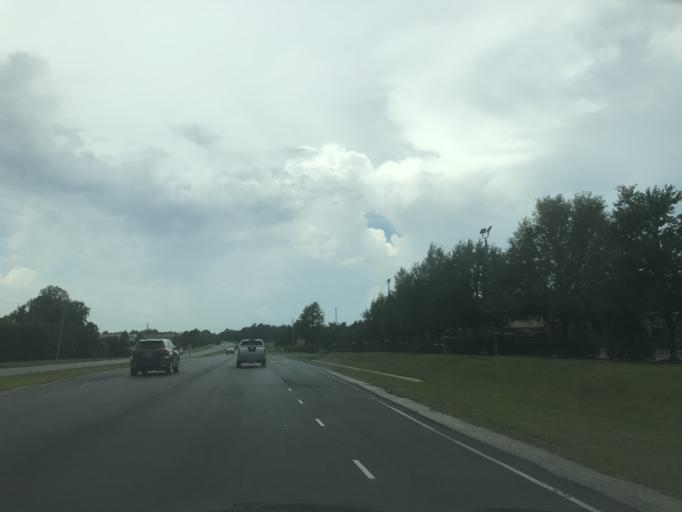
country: US
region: North Carolina
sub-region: Johnston County
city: Clayton
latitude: 35.6273
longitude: -78.4288
